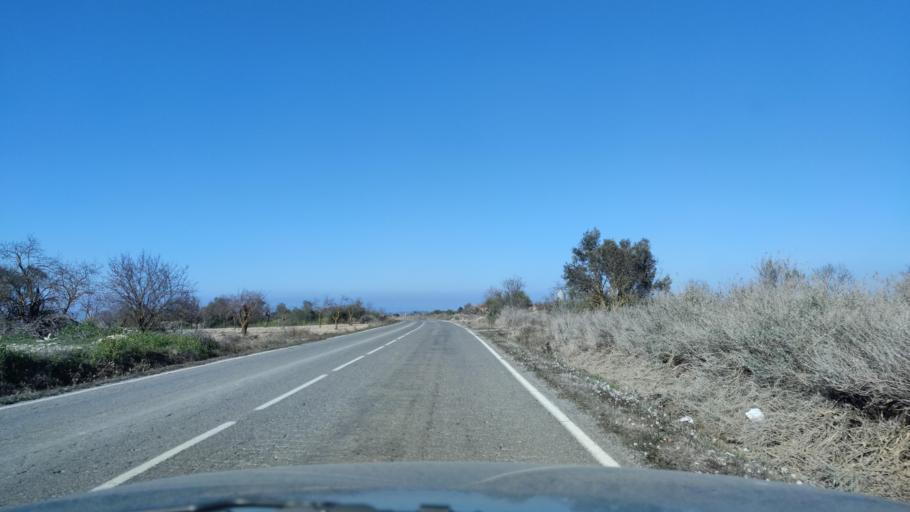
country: ES
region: Catalonia
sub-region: Provincia de Lleida
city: Maials
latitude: 41.3213
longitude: 0.4245
